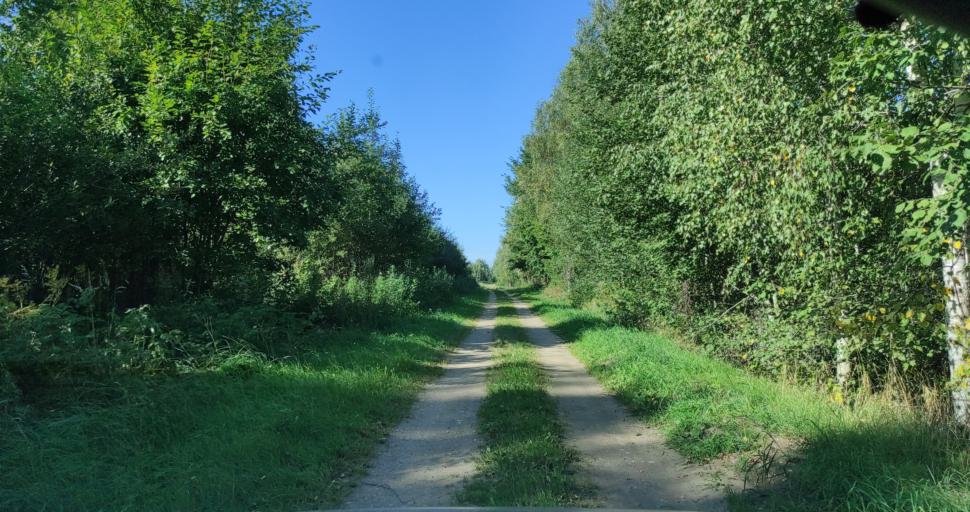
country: LV
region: Kuldigas Rajons
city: Kuldiga
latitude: 56.9743
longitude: 21.9223
